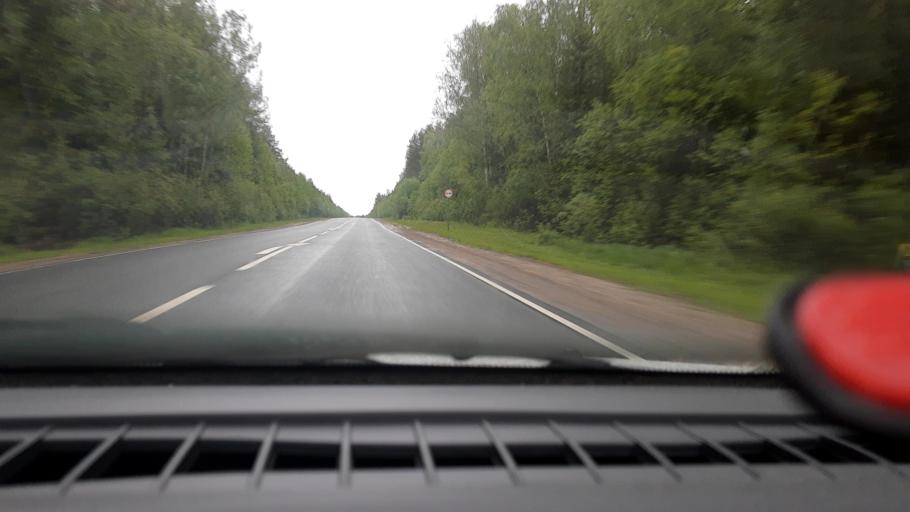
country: RU
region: Nizjnij Novgorod
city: Vladimirskoye
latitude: 56.9440
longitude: 45.0821
